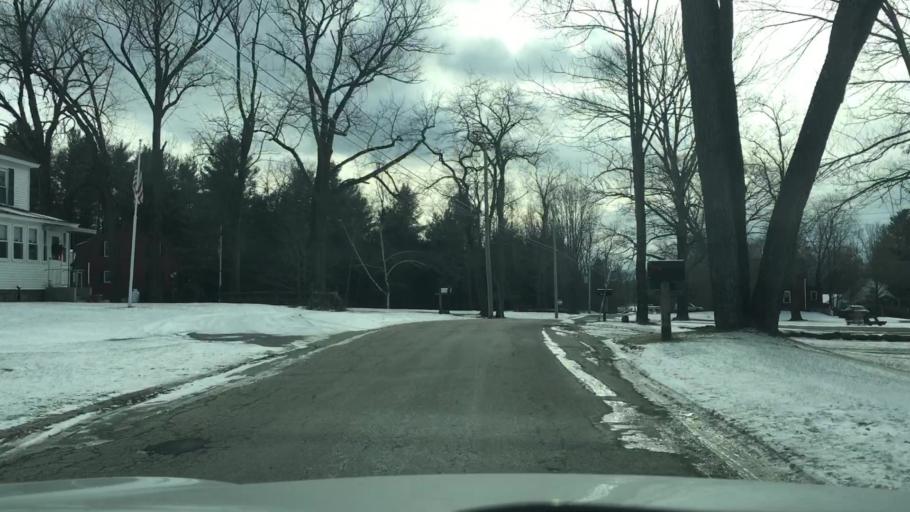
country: US
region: Massachusetts
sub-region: Berkshire County
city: Lee
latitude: 42.3336
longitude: -73.2364
